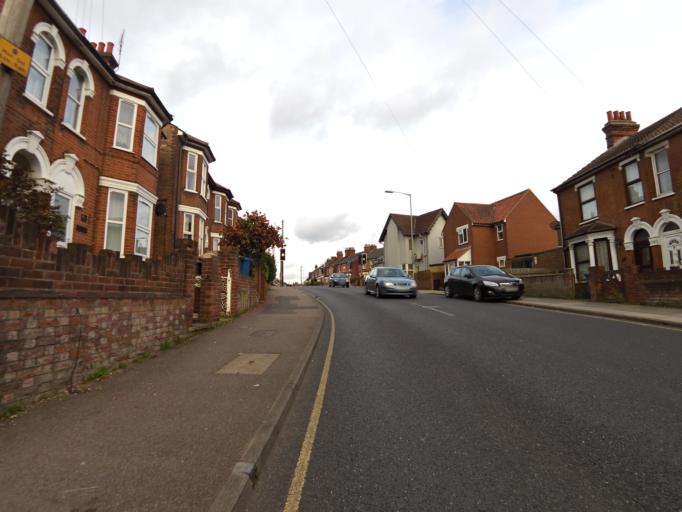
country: GB
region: England
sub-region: Suffolk
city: Ipswich
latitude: 52.0541
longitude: 1.1715
